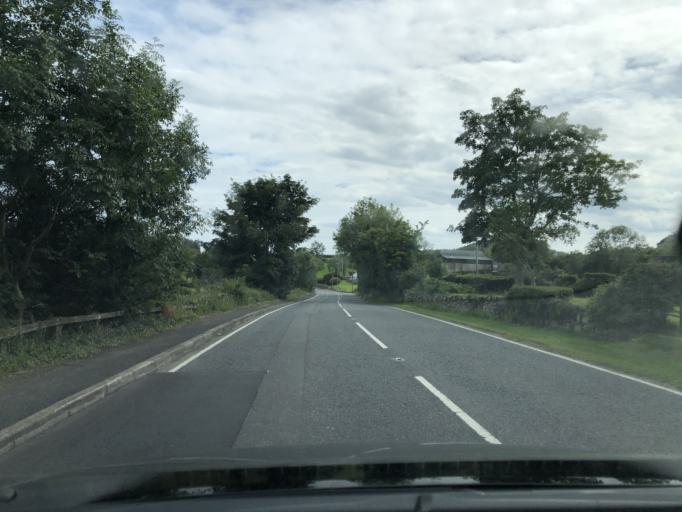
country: GB
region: Northern Ireland
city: Ballynahinch
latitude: 54.3548
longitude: -5.8550
